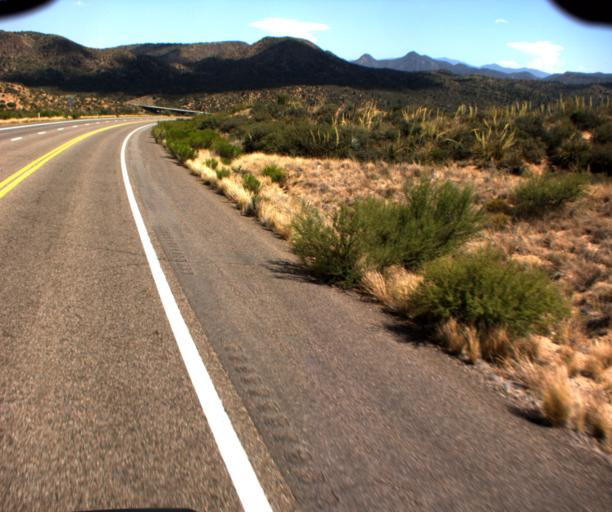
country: US
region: Arizona
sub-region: Gila County
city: Miami
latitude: 33.5316
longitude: -110.9168
